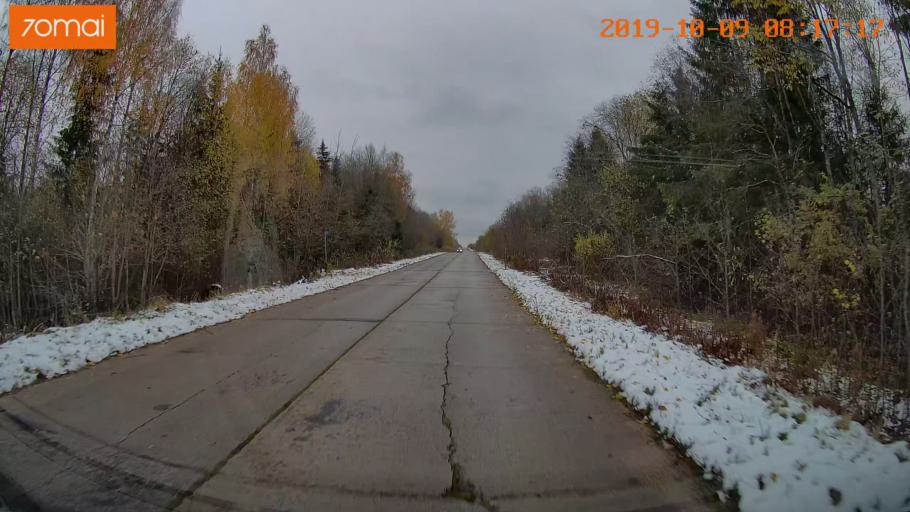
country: RU
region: Vologda
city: Gryazovets
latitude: 58.7384
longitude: 40.2026
